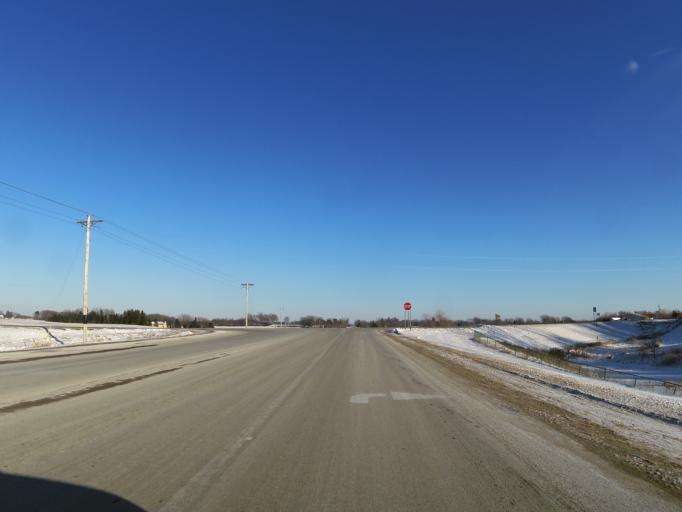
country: US
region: Minnesota
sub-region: Rice County
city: Lonsdale
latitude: 44.4863
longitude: -93.4427
